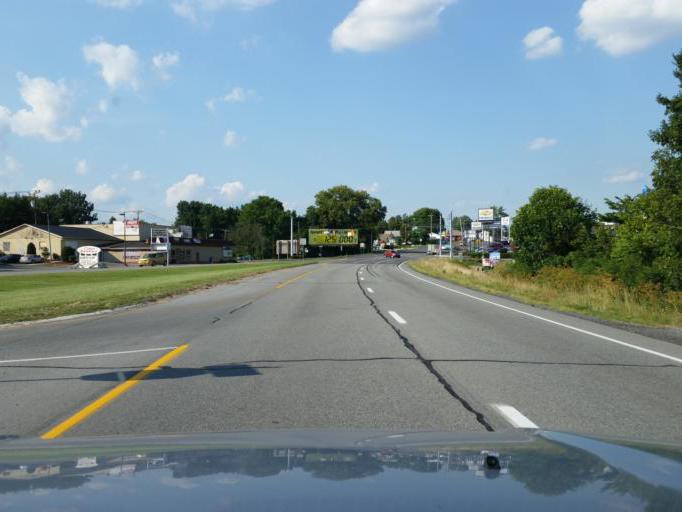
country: US
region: Pennsylvania
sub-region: Blair County
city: Altoona
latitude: 40.5144
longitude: -78.3772
